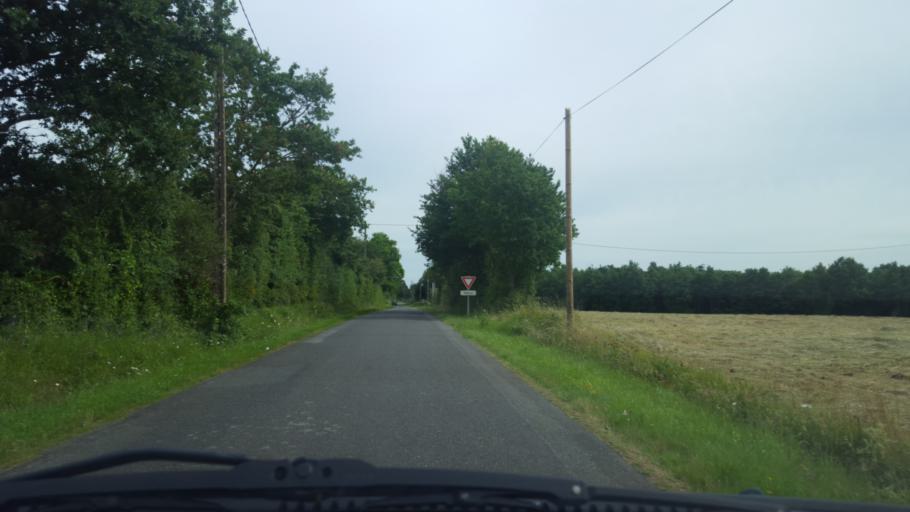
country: FR
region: Pays de la Loire
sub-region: Departement de la Loire-Atlantique
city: La Limouziniere
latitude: 46.9934
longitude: -1.5874
